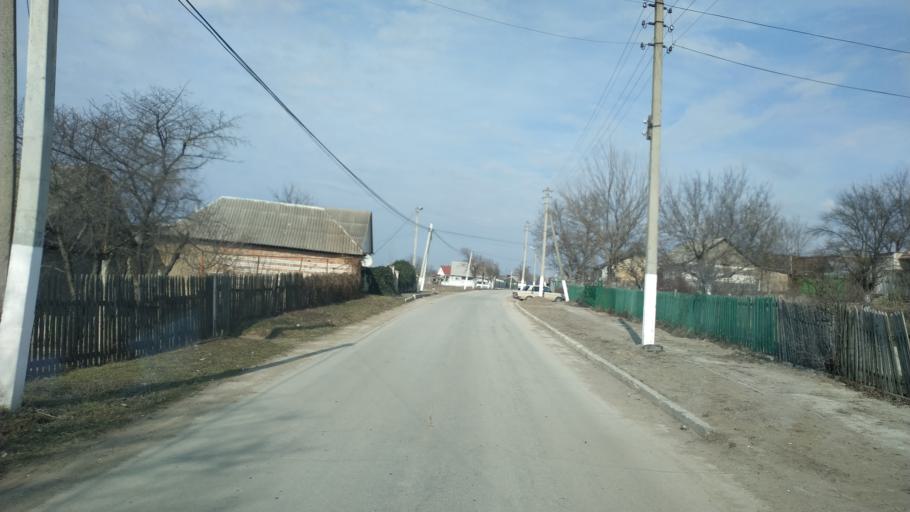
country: MD
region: Chisinau
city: Singera
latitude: 46.9264
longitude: 29.1037
